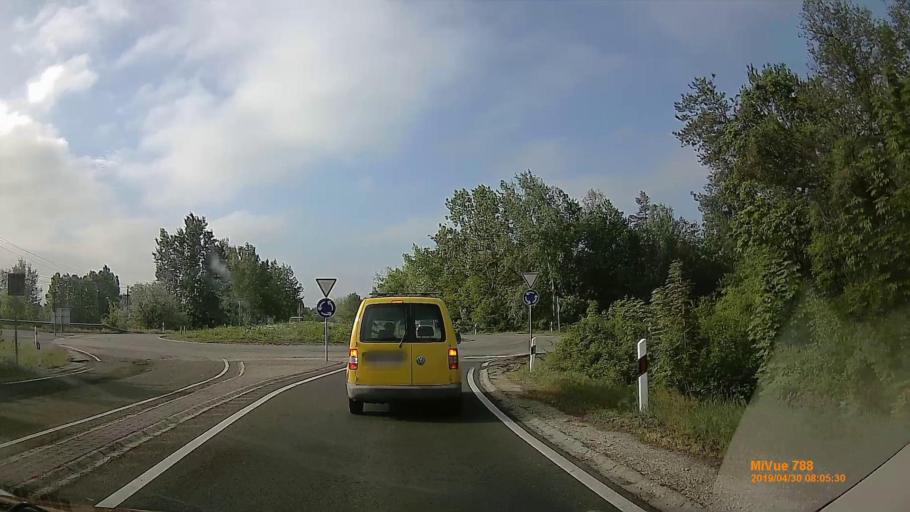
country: HU
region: Pest
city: Dunabogdany
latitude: 47.8154
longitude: 19.0926
